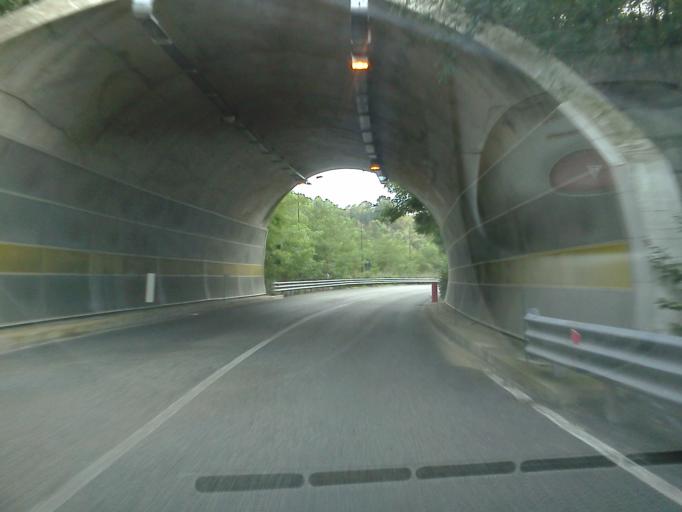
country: IT
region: Piedmont
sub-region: Provincia di Biella
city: Quaregna
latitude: 45.5865
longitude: 8.1716
